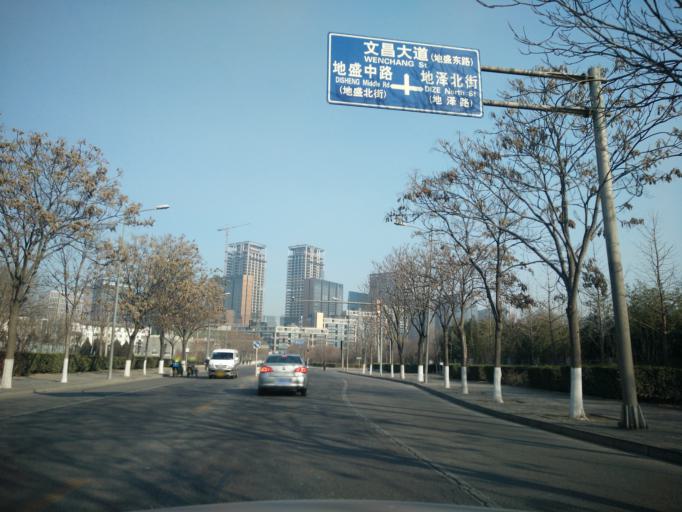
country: CN
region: Beijing
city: Jiugong
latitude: 39.7830
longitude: 116.5011
